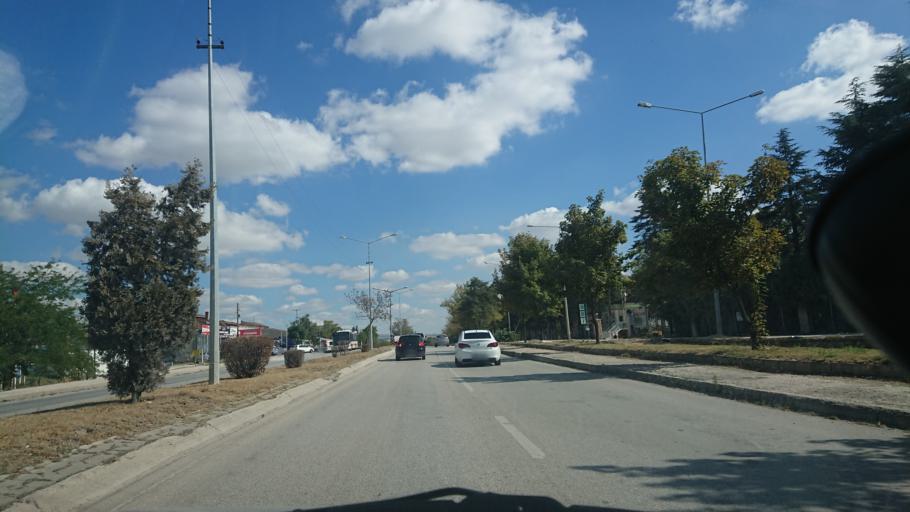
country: TR
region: Eskisehir
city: Eskisehir
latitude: 39.7616
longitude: 30.5641
